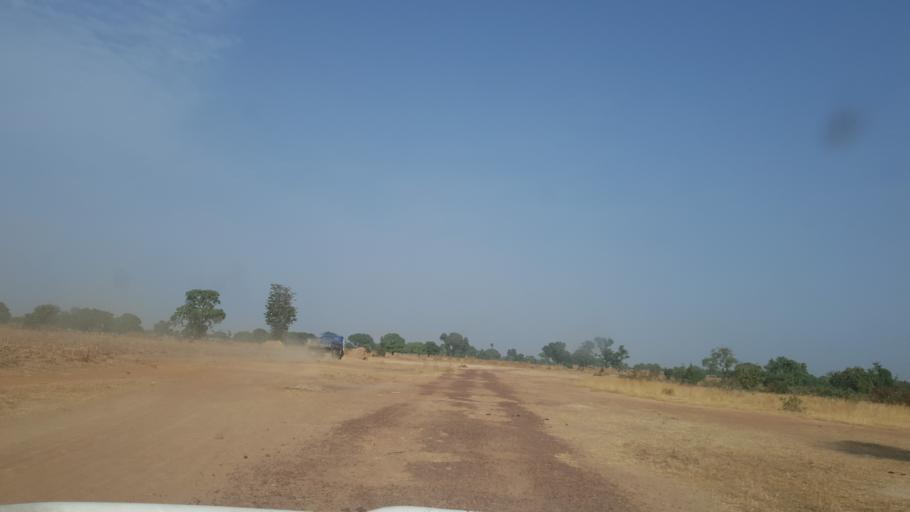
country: ML
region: Segou
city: Baroueli
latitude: 13.3523
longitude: -6.9394
